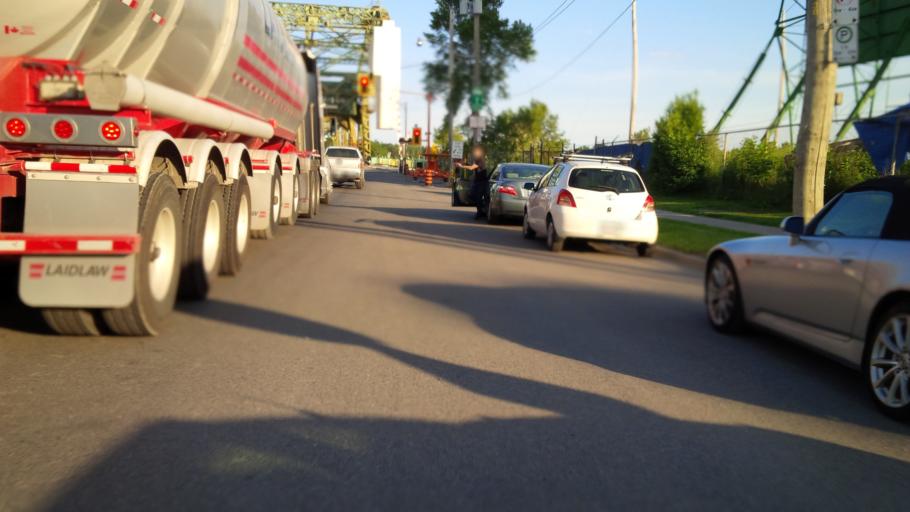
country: CA
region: Ontario
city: Toronto
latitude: 43.6423
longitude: -79.3500
